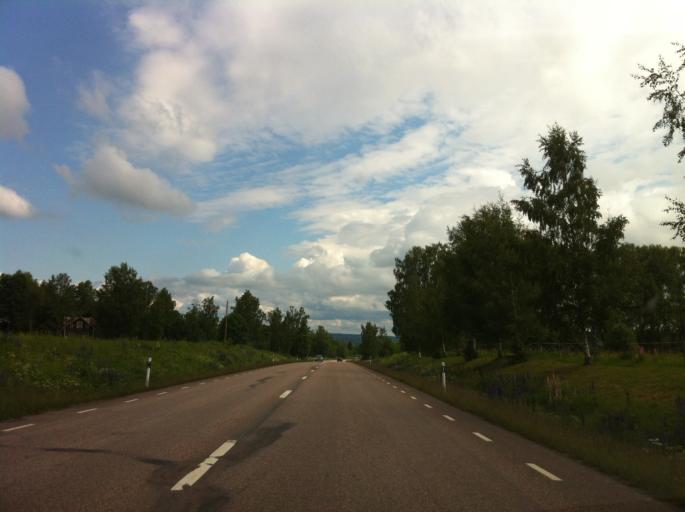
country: SE
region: Vaermland
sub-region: Sunne Kommun
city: Sunne
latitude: 59.8564
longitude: 13.1265
